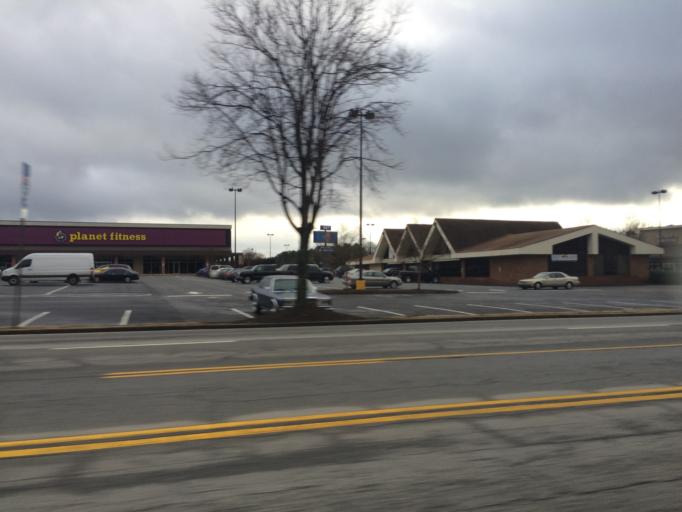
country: US
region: Georgia
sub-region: DeKalb County
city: Doraville
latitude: 33.8857
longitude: -84.2489
